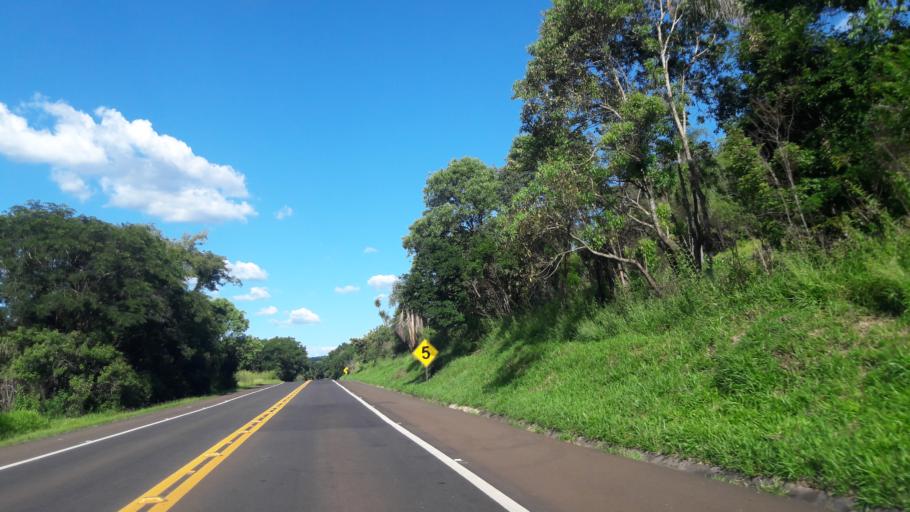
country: BR
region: Parana
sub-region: Laranjeiras Do Sul
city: Laranjeiras do Sul
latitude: -25.4210
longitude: -52.0400
